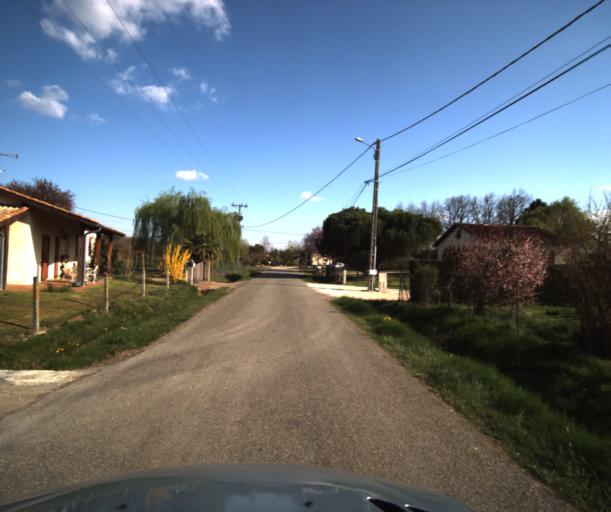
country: FR
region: Midi-Pyrenees
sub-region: Departement du Tarn-et-Garonne
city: Campsas
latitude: 43.9345
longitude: 1.3071
